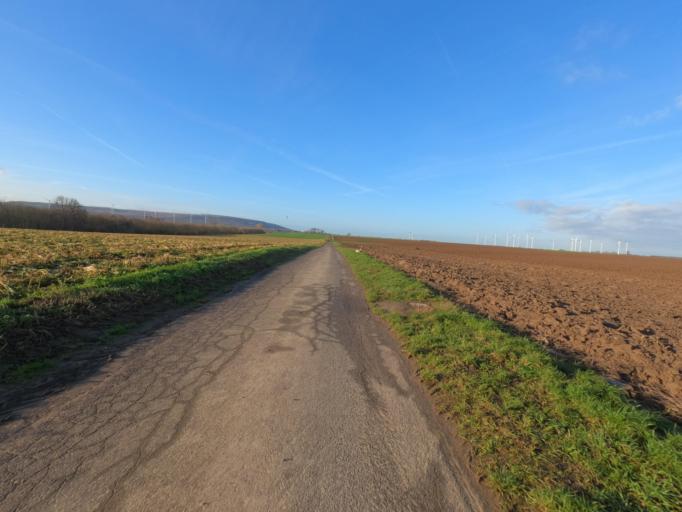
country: DE
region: North Rhine-Westphalia
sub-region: Regierungsbezirk Koln
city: Elsdorf
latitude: 50.9660
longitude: 6.5284
